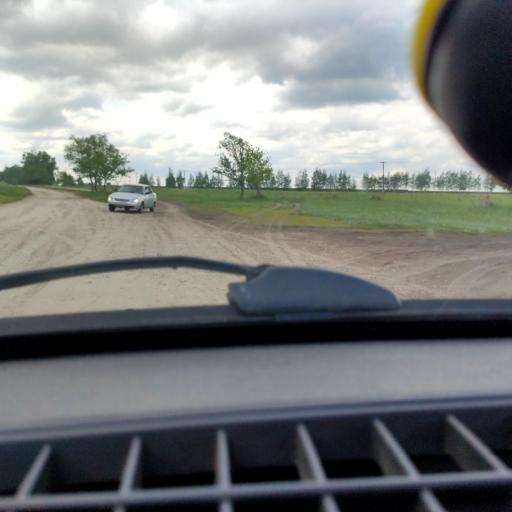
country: RU
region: Samara
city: Povolzhskiy
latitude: 53.6321
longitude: 49.6639
